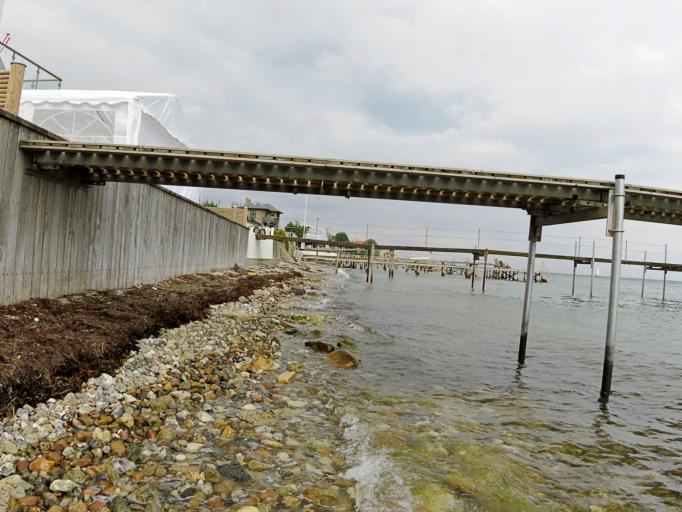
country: DK
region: Capital Region
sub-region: Gentofte Kommune
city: Charlottenlund
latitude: 55.7826
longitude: 12.5937
